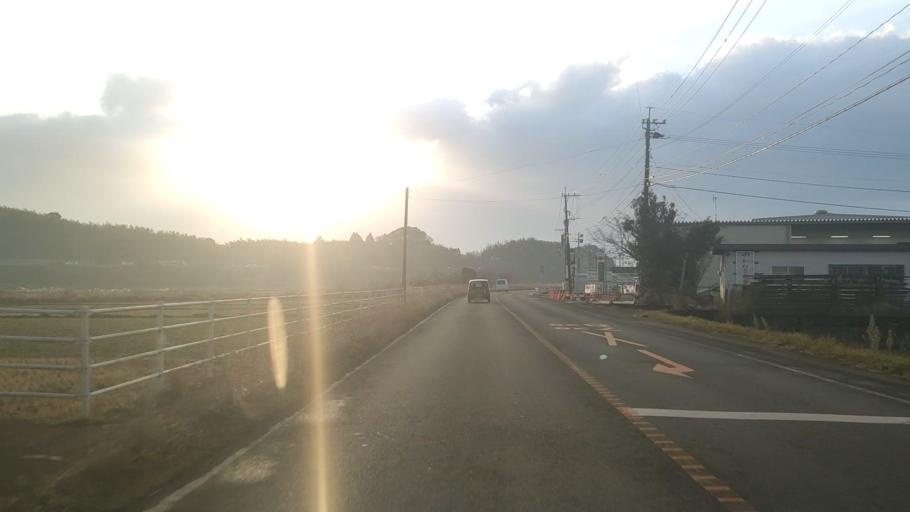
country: JP
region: Kumamoto
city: Uto
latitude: 32.7240
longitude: 130.7672
